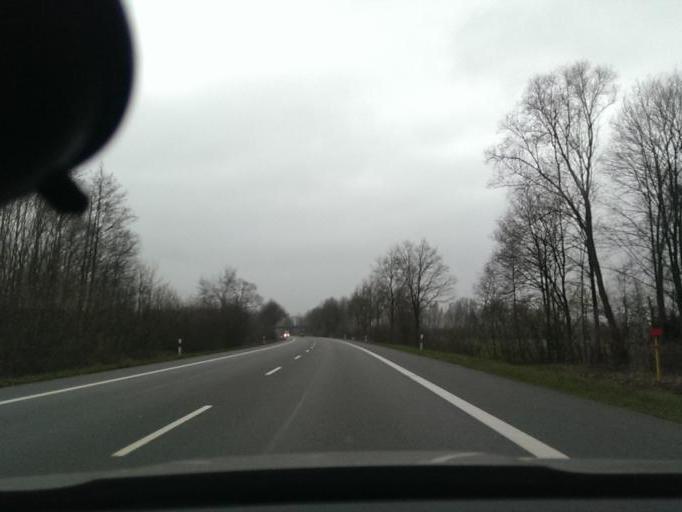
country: DE
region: North Rhine-Westphalia
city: Rietberg
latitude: 51.7991
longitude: 8.4126
